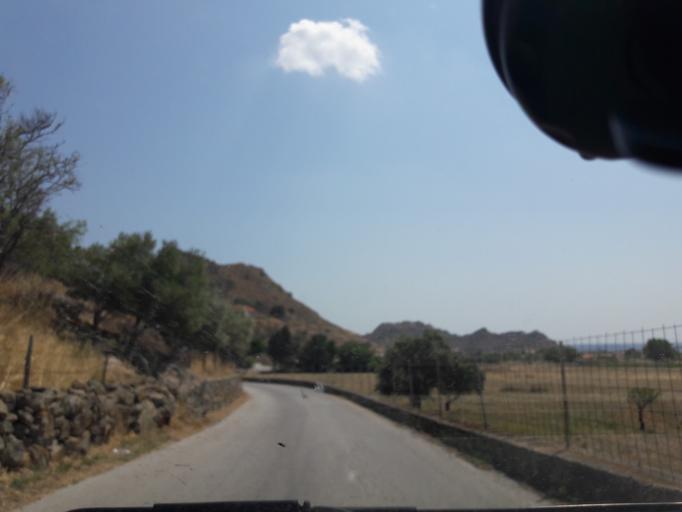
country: GR
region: North Aegean
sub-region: Nomos Lesvou
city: Myrina
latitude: 39.8483
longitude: 25.0847
